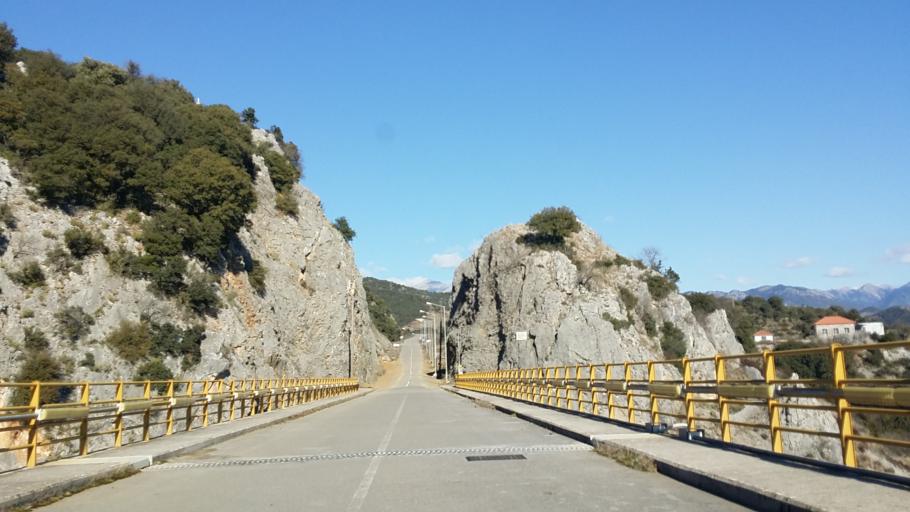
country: GR
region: Central Greece
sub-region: Nomos Evrytanias
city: Kerasochori
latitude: 38.9721
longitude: 21.4920
